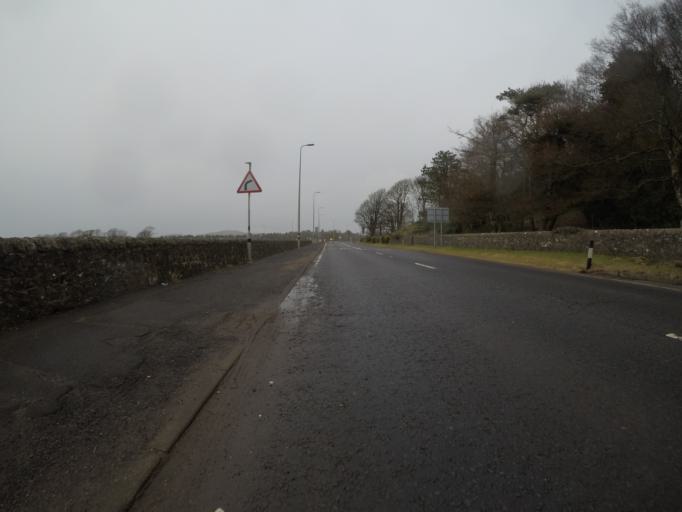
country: GB
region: Scotland
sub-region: North Ayrshire
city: West Kilbride
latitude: 55.6944
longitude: -4.8675
